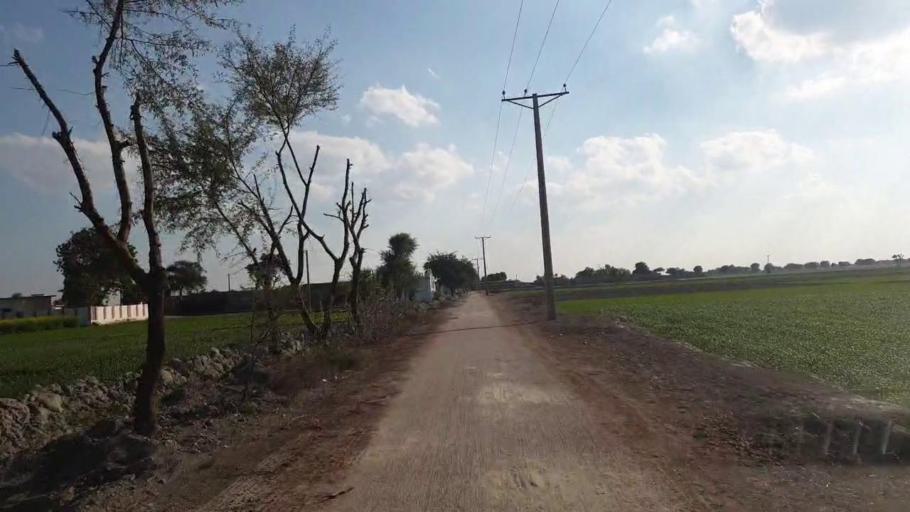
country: PK
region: Sindh
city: Shahpur Chakar
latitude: 26.1049
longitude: 68.5825
